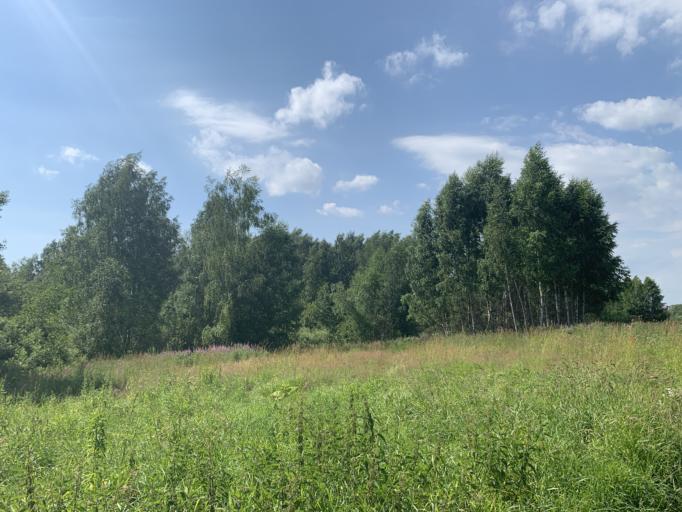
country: RU
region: Moskovskaya
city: Cherkizovo
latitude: 55.9744
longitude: 37.8004
